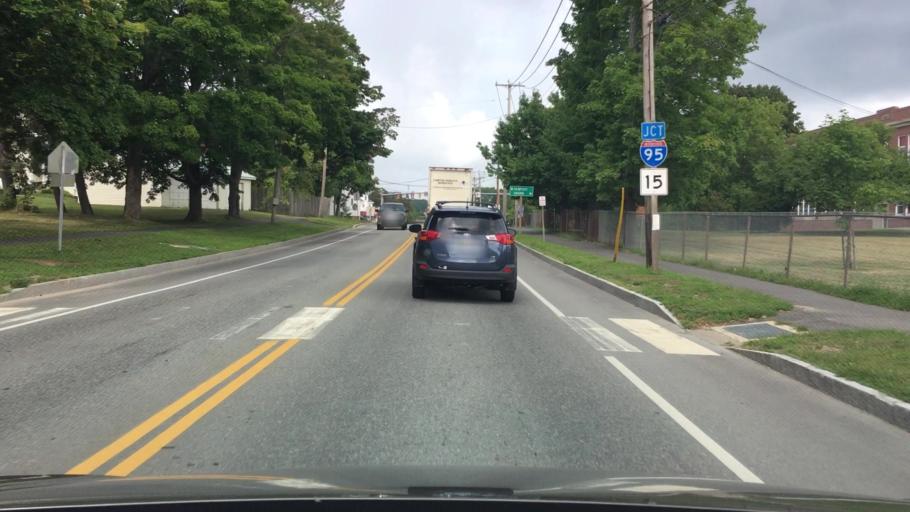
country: US
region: Maine
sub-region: Penobscot County
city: Bangor
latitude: 44.8166
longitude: -68.7727
